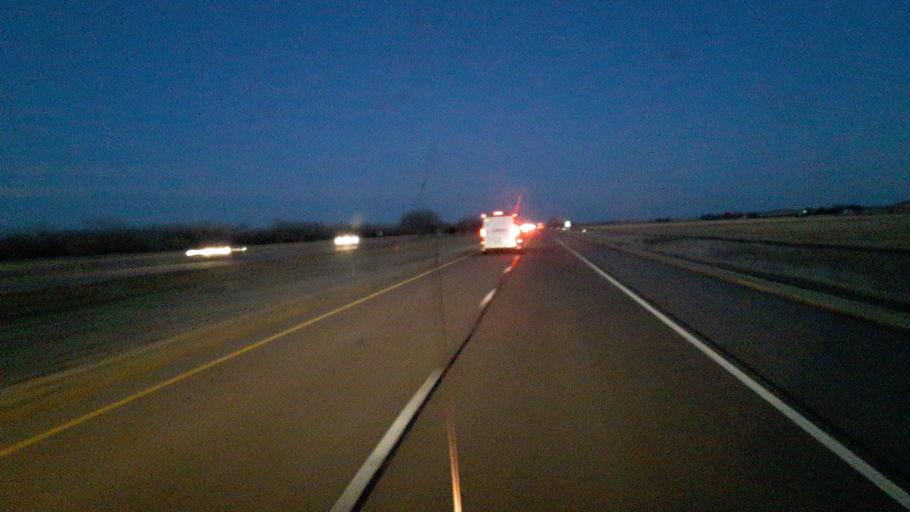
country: US
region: Nebraska
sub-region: Lincoln County
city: Sutherland
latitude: 41.1145
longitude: -101.3141
